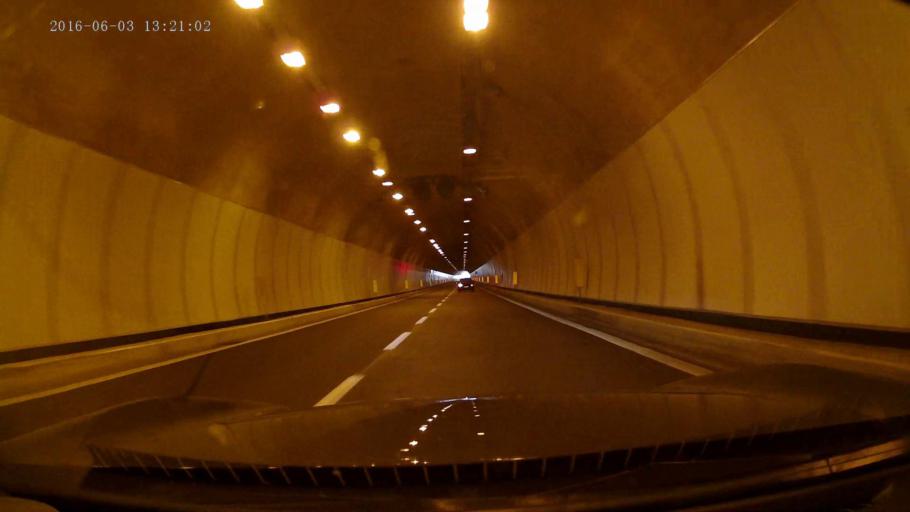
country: IT
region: Trentino-Alto Adige
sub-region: Bolzano
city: Fie Allo Sciliar
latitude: 46.5251
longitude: 11.4870
